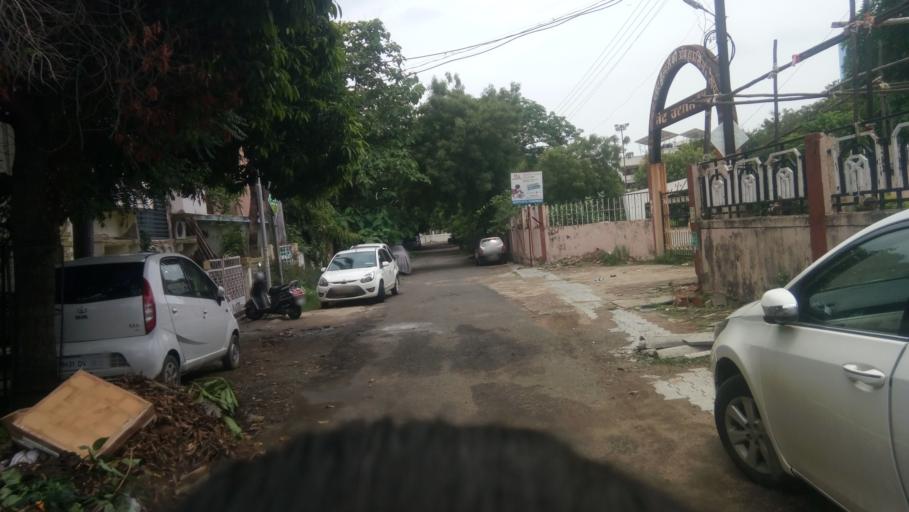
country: IN
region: Maharashtra
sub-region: Nagpur Division
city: Nagpur
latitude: 21.1083
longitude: 79.0636
